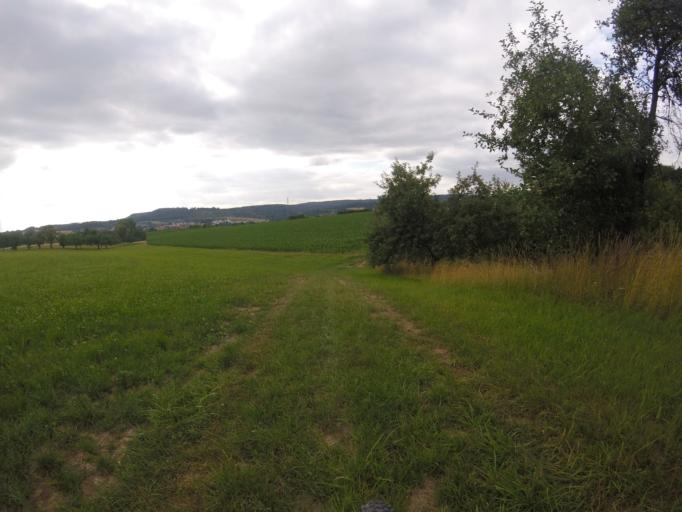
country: DE
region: Baden-Wuerttemberg
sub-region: Regierungsbezirk Stuttgart
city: Oppenweiler
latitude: 48.9801
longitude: 9.4745
